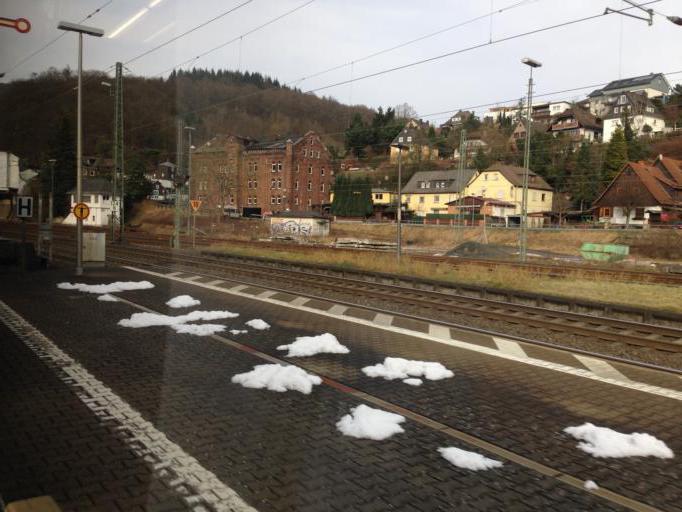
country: DE
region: Hesse
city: Dillenburg
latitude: 50.7363
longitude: 8.2941
